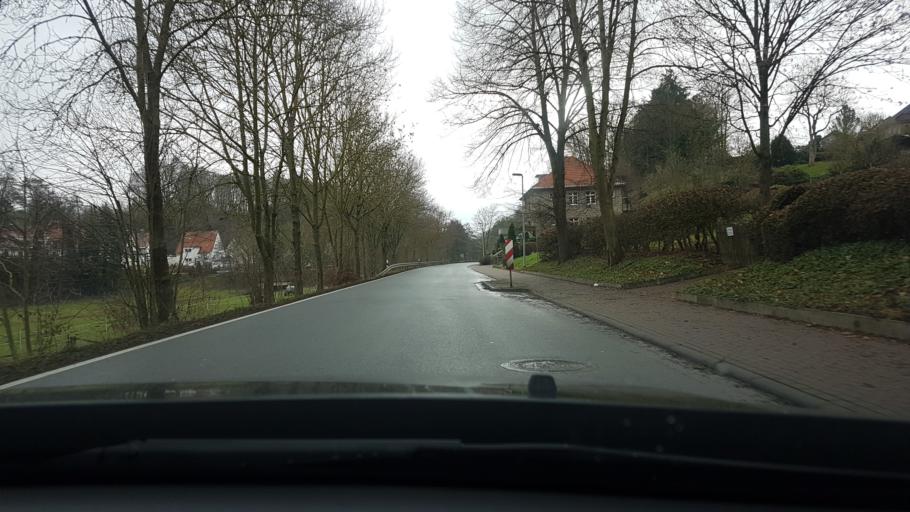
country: DE
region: North Rhine-Westphalia
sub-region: Regierungsbezirk Detmold
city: Willebadessen
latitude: 51.5075
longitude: 8.9991
